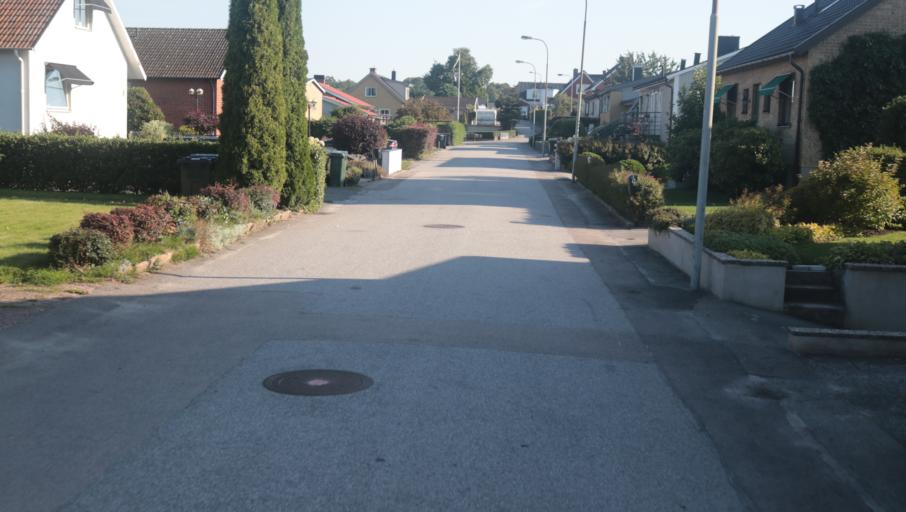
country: SE
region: Blekinge
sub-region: Karlshamns Kommun
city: Karlshamn
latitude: 56.1849
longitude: 14.8516
